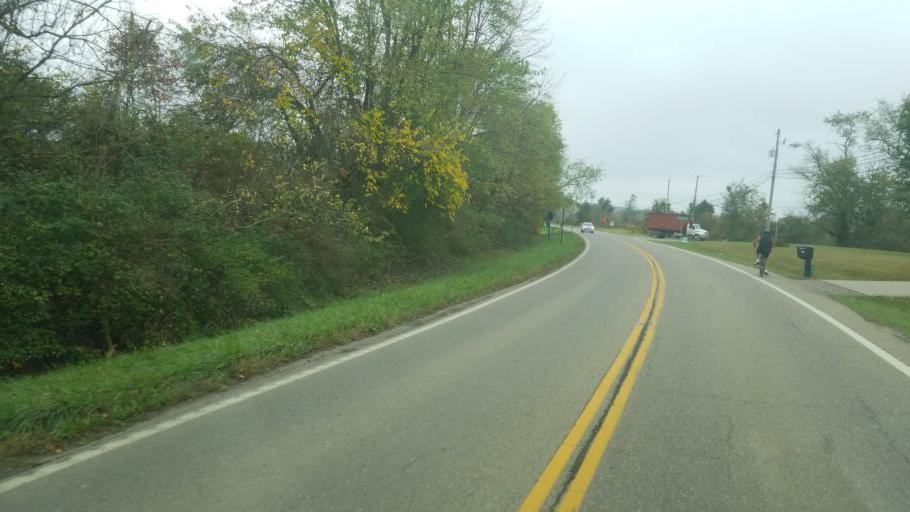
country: US
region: Ohio
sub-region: Tuscarawas County
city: Strasburg
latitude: 40.6545
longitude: -81.4723
